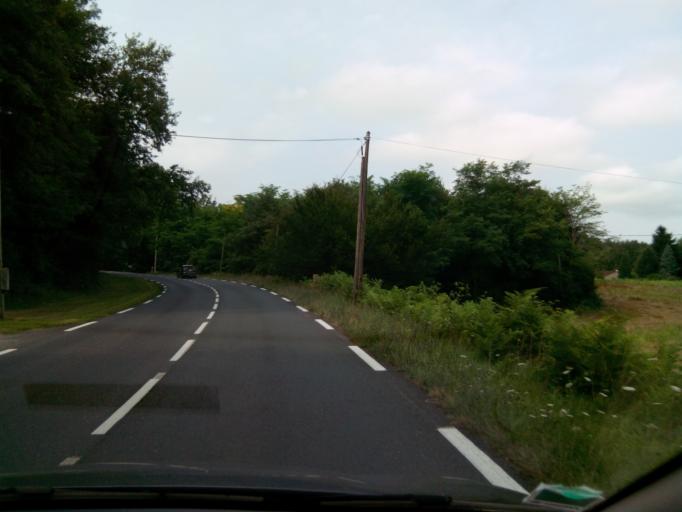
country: FR
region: Aquitaine
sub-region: Departement de la Dordogne
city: Carsac-Aillac
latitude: 44.8670
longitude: 1.2685
